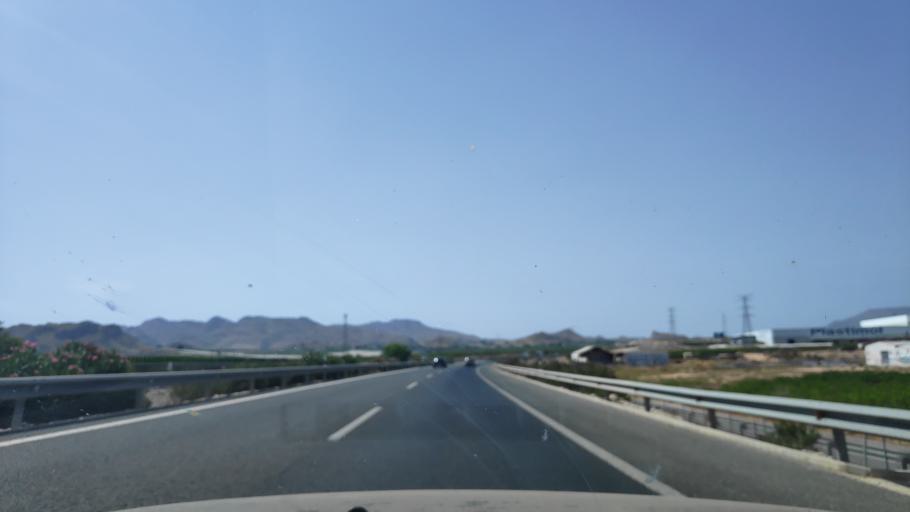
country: ES
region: Murcia
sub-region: Murcia
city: Archena
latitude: 38.1336
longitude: -1.2678
